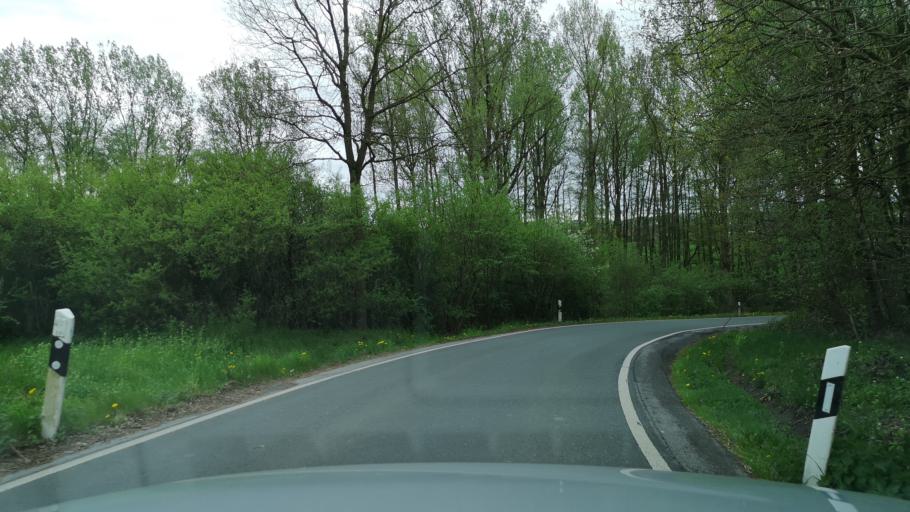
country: DE
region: North Rhine-Westphalia
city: Iserlohn
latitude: 51.4416
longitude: 7.7109
